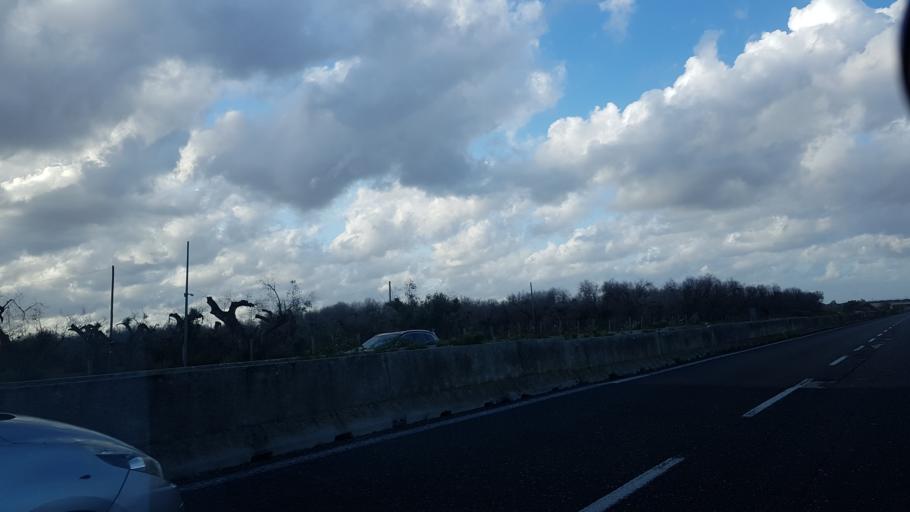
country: IT
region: Apulia
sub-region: Provincia di Brindisi
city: Torchiarolo
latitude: 40.4801
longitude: 18.0450
